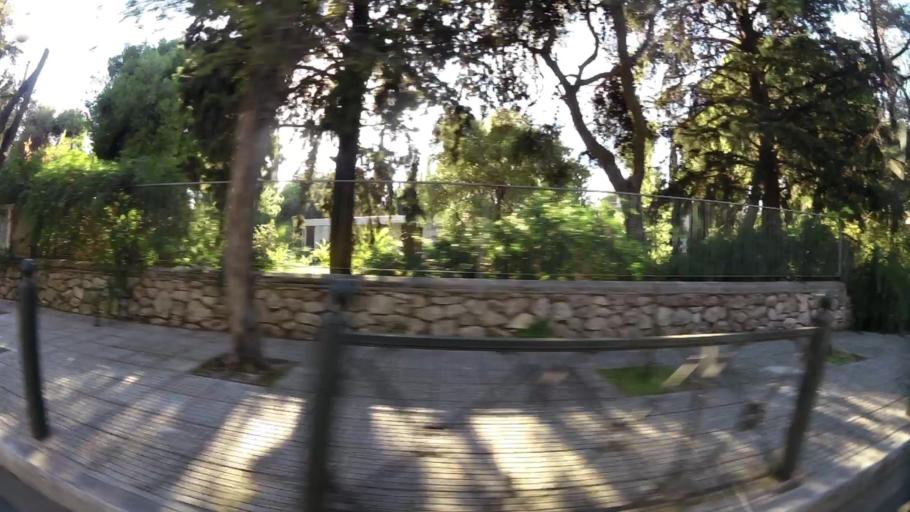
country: GR
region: Attica
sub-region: Nomarchia Athinas
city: Kifisia
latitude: 38.0806
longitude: 23.8112
